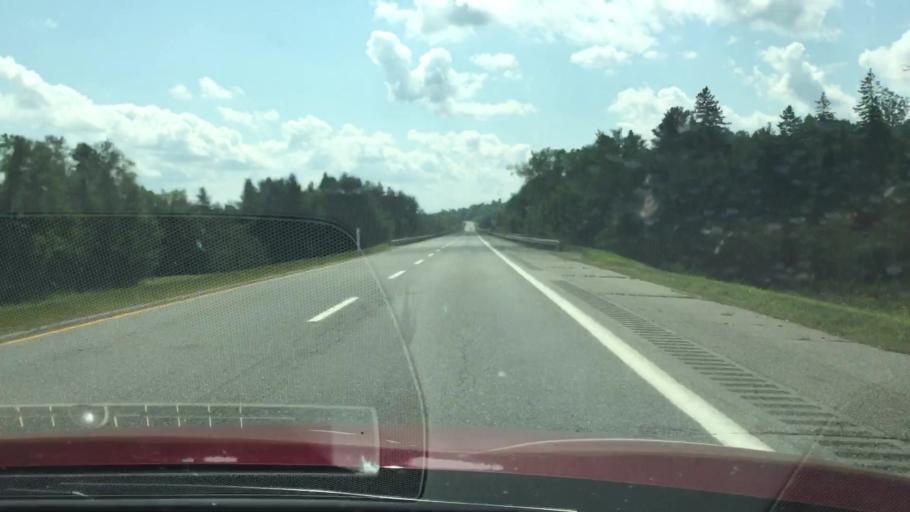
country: US
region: Maine
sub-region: Penobscot County
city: Lincoln
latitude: 45.4715
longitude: -68.5807
